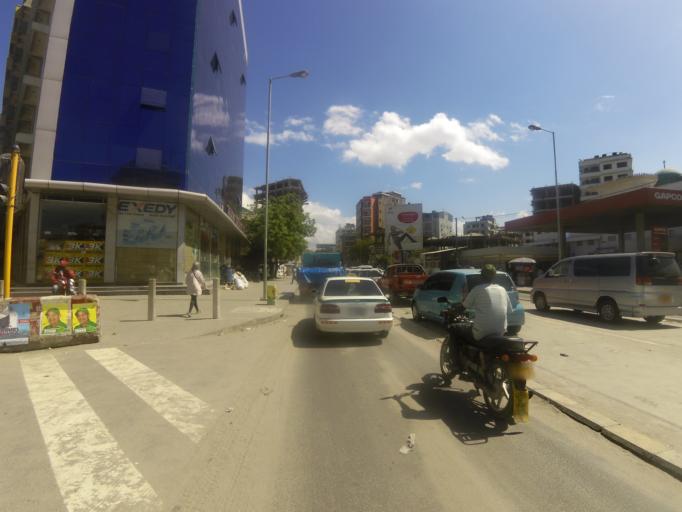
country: TZ
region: Dar es Salaam
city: Dar es Salaam
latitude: -6.8169
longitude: 39.2743
